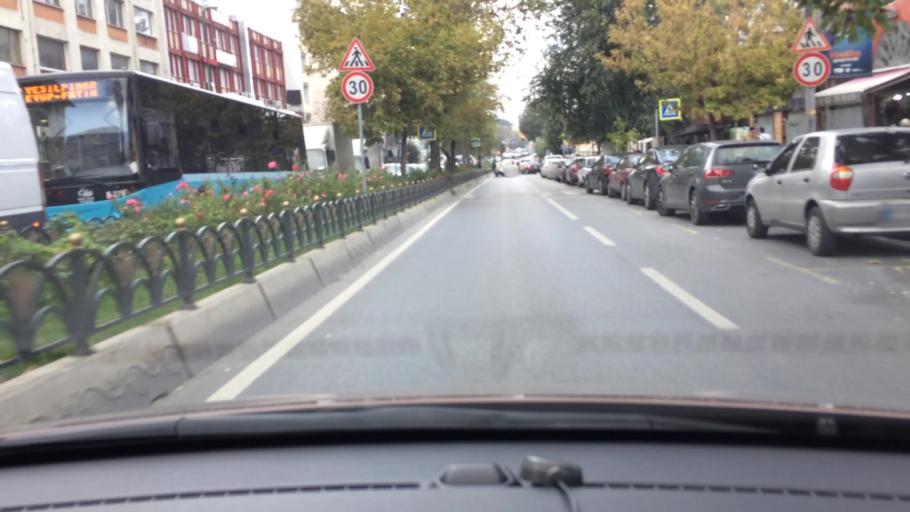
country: TR
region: Istanbul
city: Istanbul
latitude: 41.0125
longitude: 28.9587
